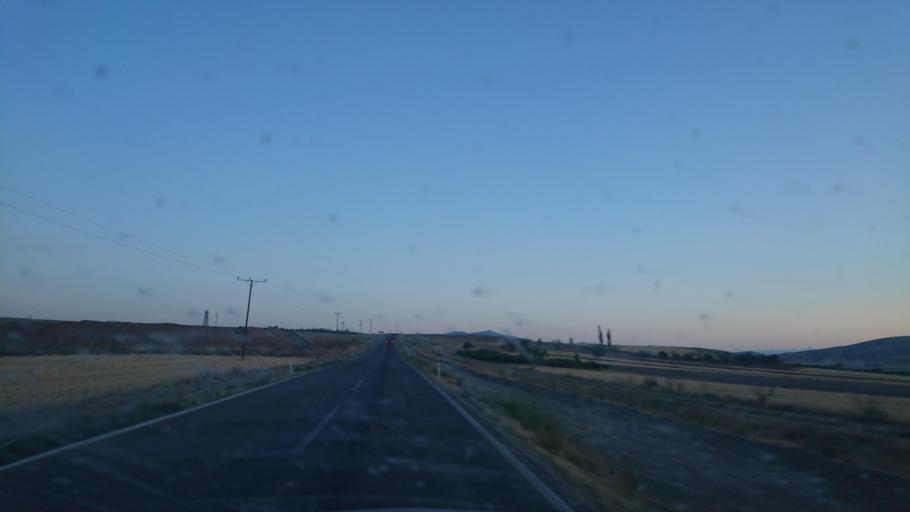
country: TR
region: Aksaray
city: Balci
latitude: 38.8045
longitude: 34.1307
